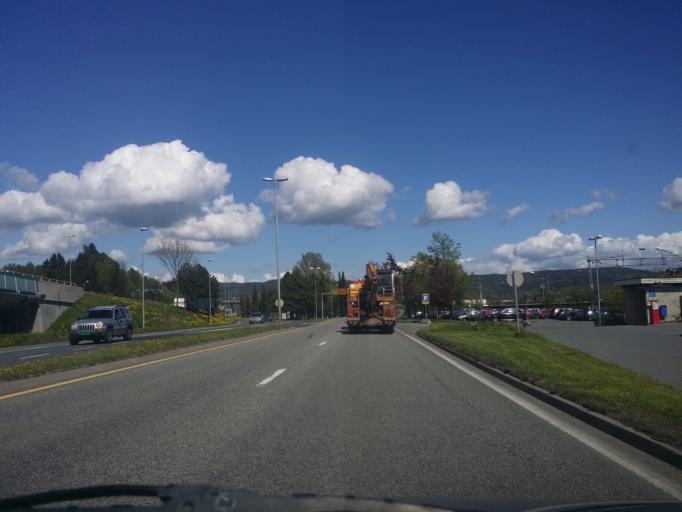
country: NO
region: Buskerud
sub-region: Drammen
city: Drammen
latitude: 59.7437
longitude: 10.2314
